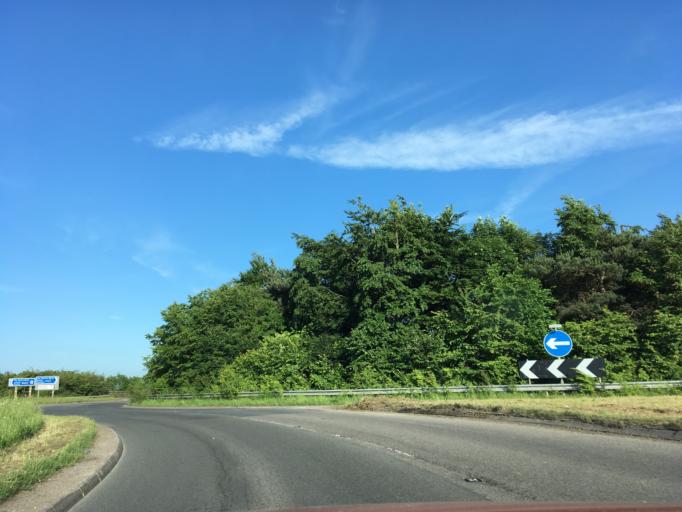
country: GB
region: England
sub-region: Somerset
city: North Petherton
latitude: 51.1026
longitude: -2.9953
